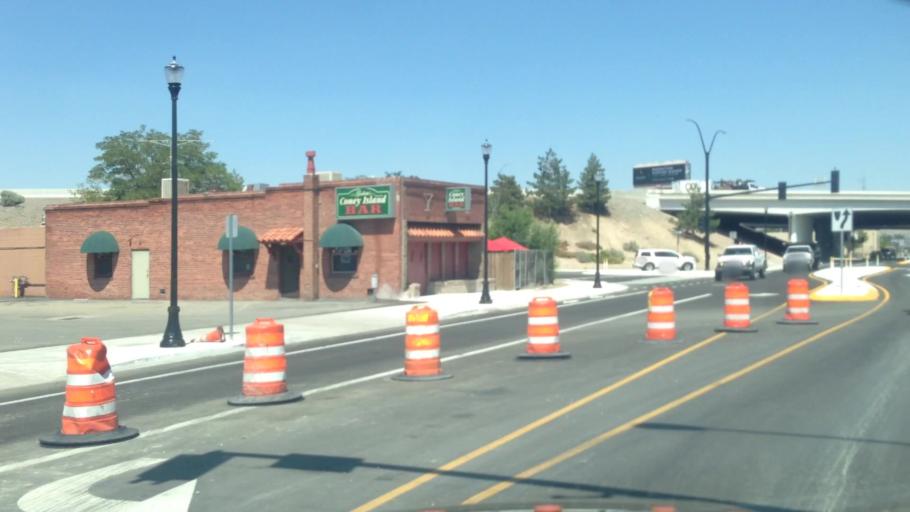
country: US
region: Nevada
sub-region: Washoe County
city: Sparks
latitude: 39.5351
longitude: -119.7806
